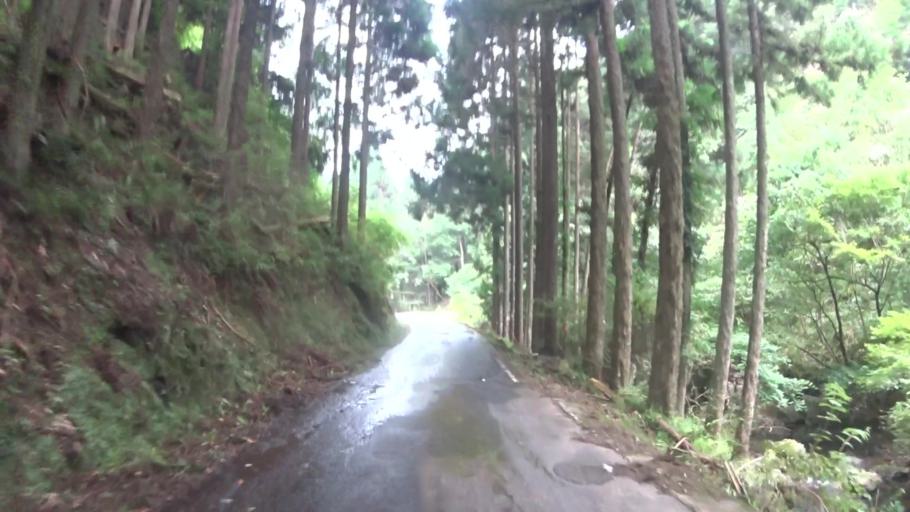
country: JP
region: Kyoto
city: Kameoka
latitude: 35.1589
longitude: 135.5720
